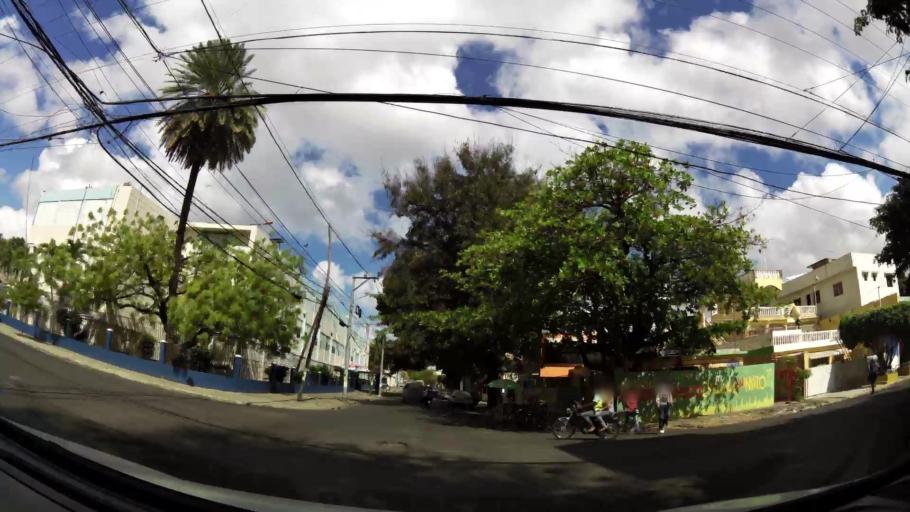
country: DO
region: Nacional
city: Ensanche Luperon
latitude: 18.4927
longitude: -69.8877
